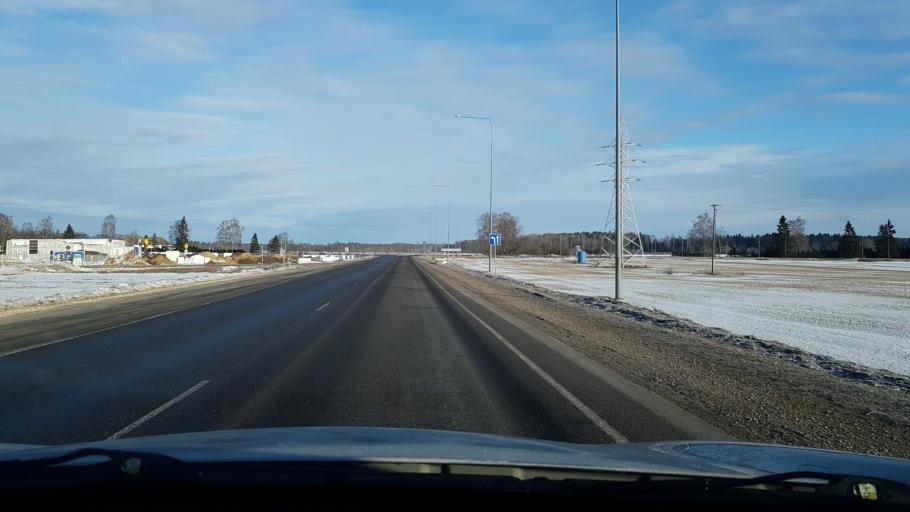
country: EE
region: Jogevamaa
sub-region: Poltsamaa linn
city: Poltsamaa
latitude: 58.7432
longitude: 25.7691
